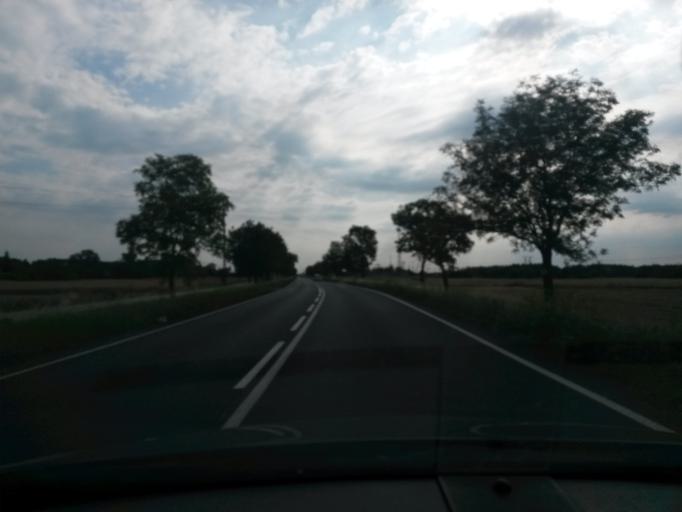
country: PL
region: Greater Poland Voivodeship
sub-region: Powiat rawicki
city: Rawicz
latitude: 51.6248
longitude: 16.8862
